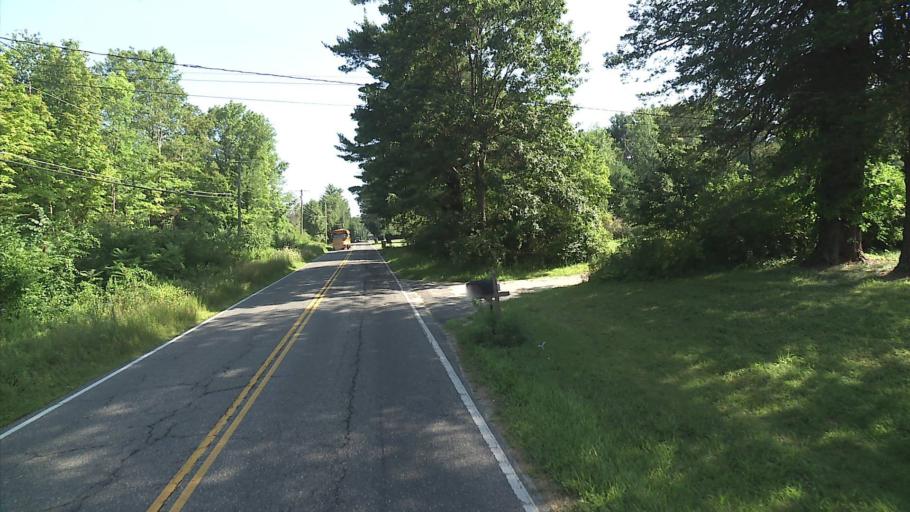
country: US
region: Connecticut
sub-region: Litchfield County
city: Winsted
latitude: 41.8724
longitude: -73.0677
